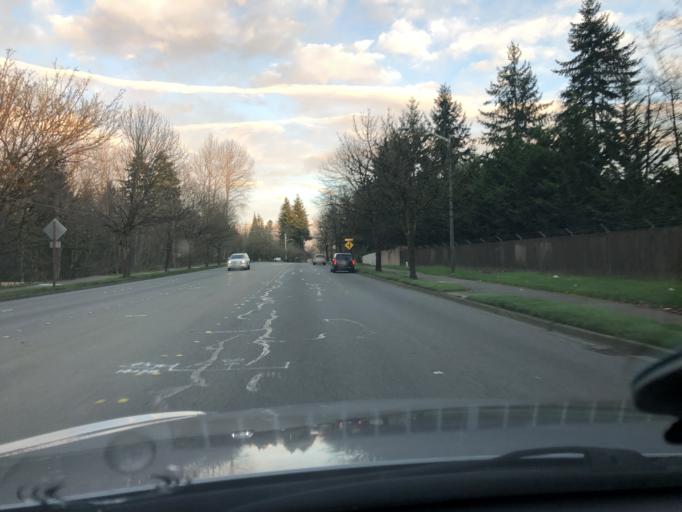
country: US
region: Washington
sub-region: King County
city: Federal Way
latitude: 47.3152
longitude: -122.3472
